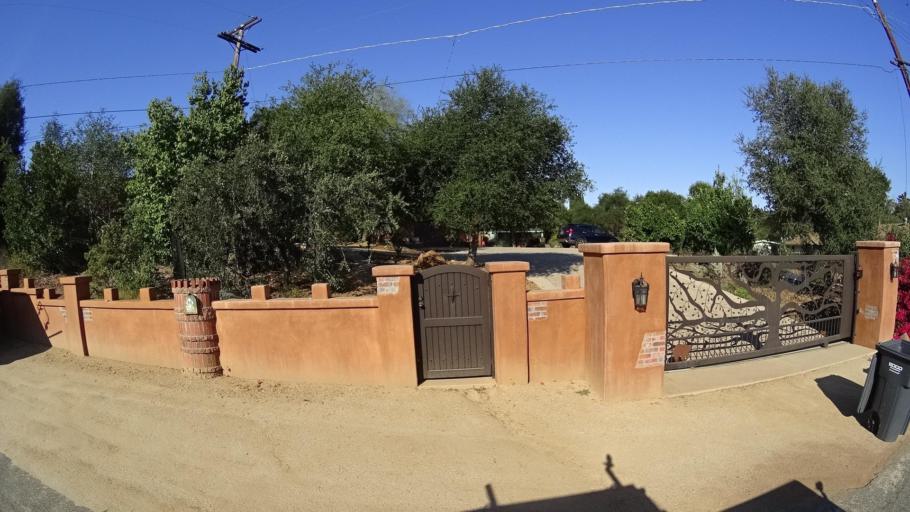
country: US
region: California
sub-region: San Diego County
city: Escondido
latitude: 33.0857
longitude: -117.0856
